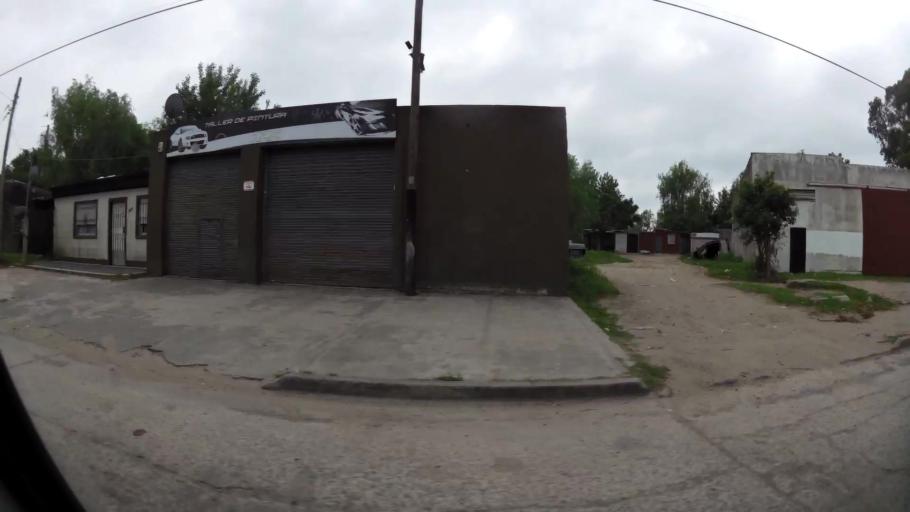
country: AR
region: Buenos Aires
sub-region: Partido de La Plata
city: La Plata
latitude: -34.8807
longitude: -57.9691
